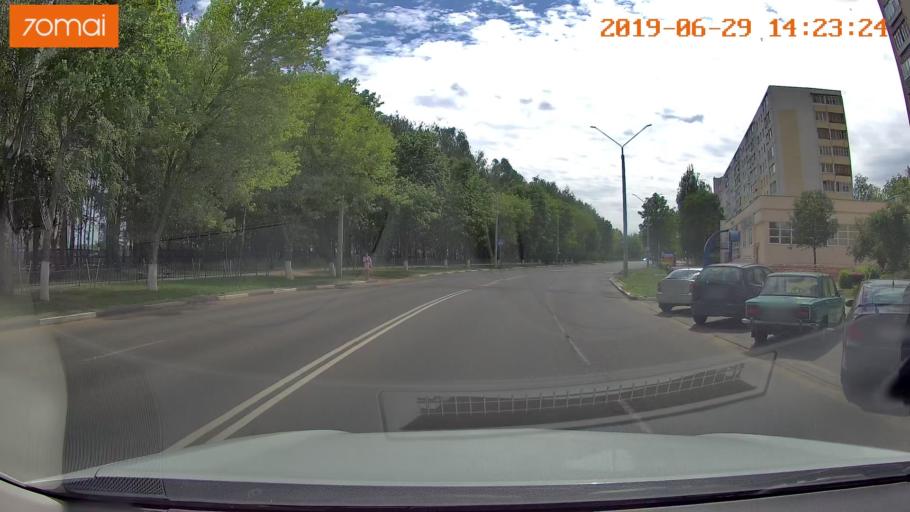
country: BY
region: Minsk
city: Salihorsk
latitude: 52.7860
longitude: 27.5544
